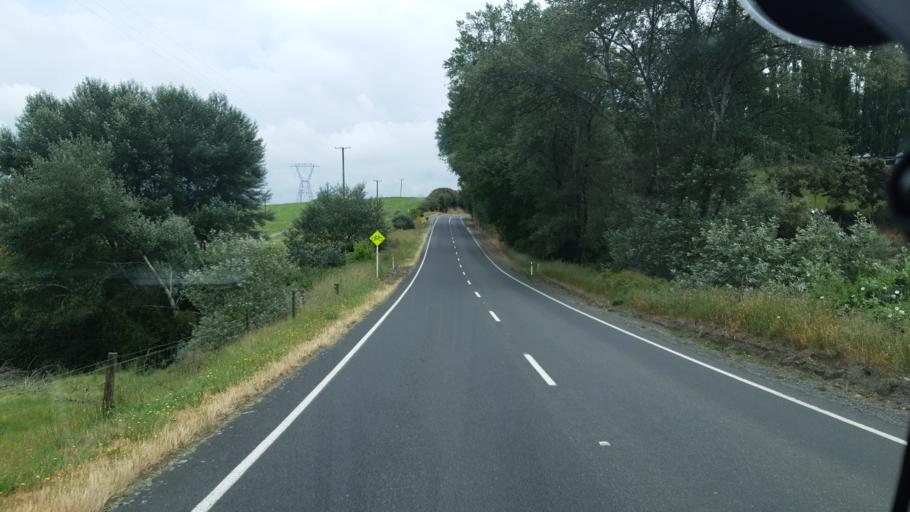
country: NZ
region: Waikato
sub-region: South Waikato District
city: Tokoroa
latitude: -38.4001
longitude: 175.7686
